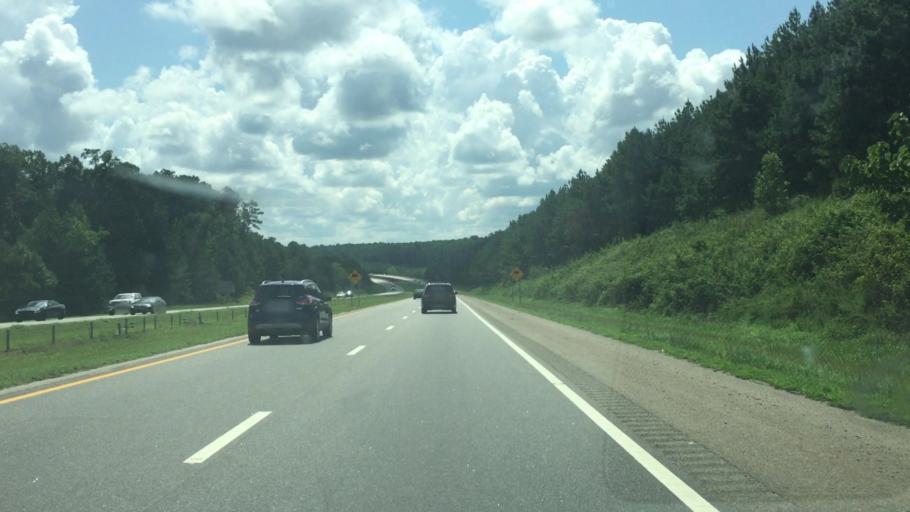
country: US
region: North Carolina
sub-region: Richmond County
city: Cordova
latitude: 34.9261
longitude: -79.8201
